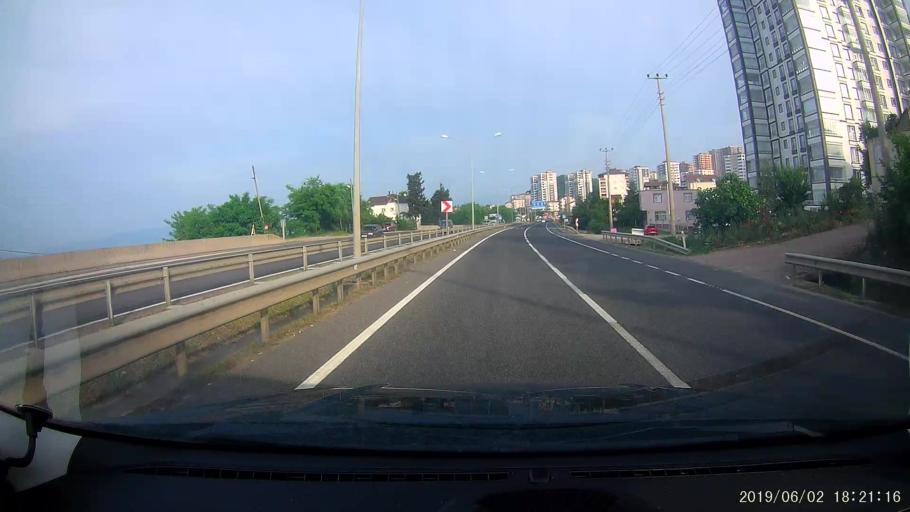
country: TR
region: Ordu
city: Fatsa
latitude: 41.0669
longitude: 37.4668
